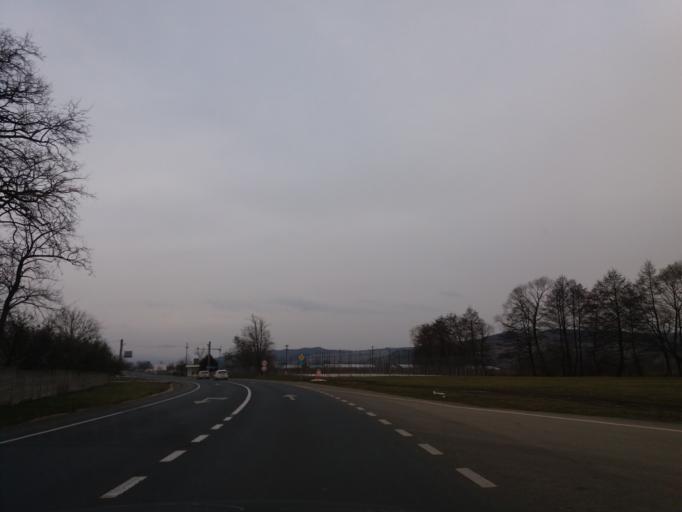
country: RO
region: Hunedoara
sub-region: Comuna Bacia
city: Bacia
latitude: 45.7998
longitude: 23.0092
